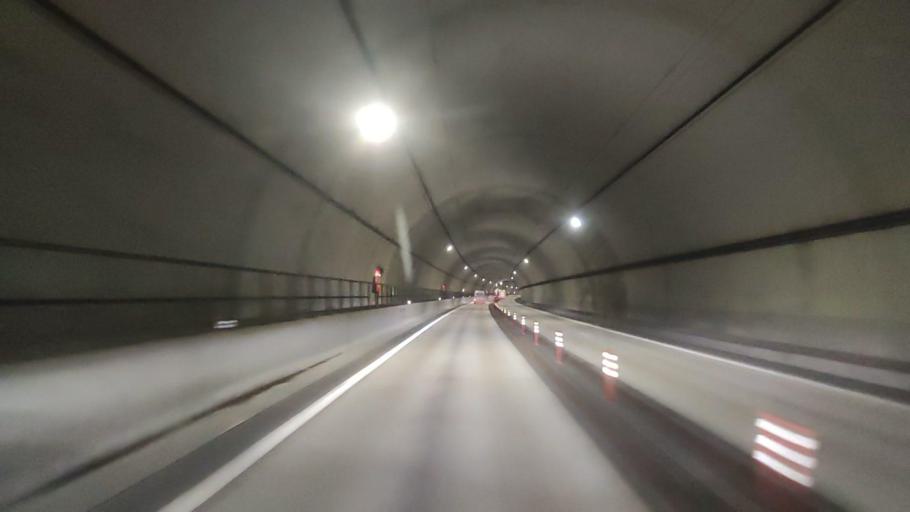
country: JP
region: Wakayama
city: Tanabe
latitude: 33.5915
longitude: 135.4389
